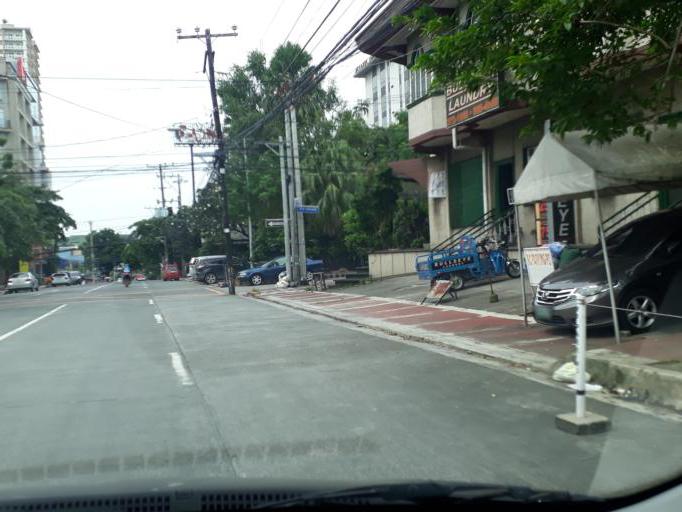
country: PH
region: Calabarzon
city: Del Monte
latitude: 14.6304
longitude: 121.0321
